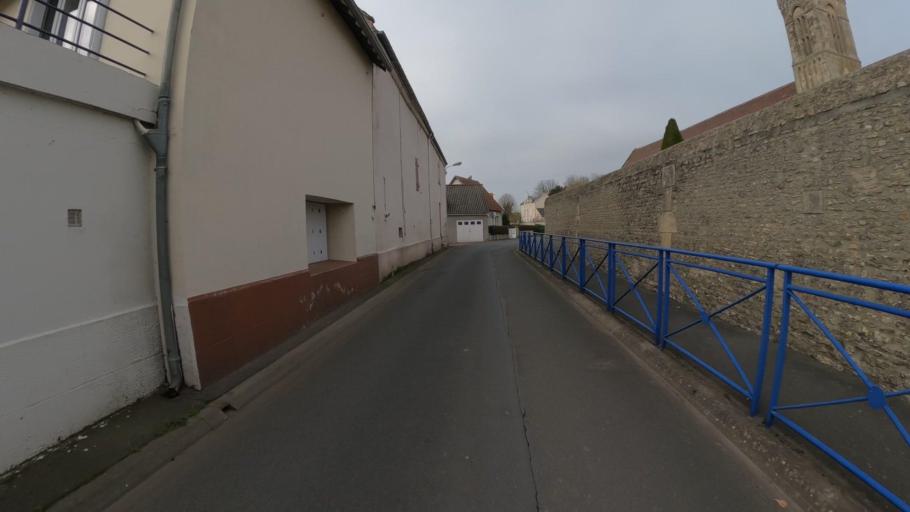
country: FR
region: Lower Normandy
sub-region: Departement du Calvados
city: Authie
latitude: 49.2068
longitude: -0.4320
